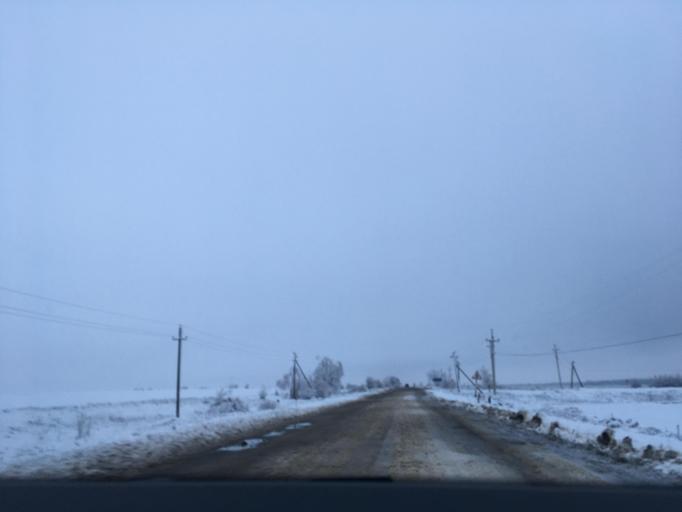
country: RU
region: Voronezj
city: Verkhniy Mamon
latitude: 50.0286
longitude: 40.0709
